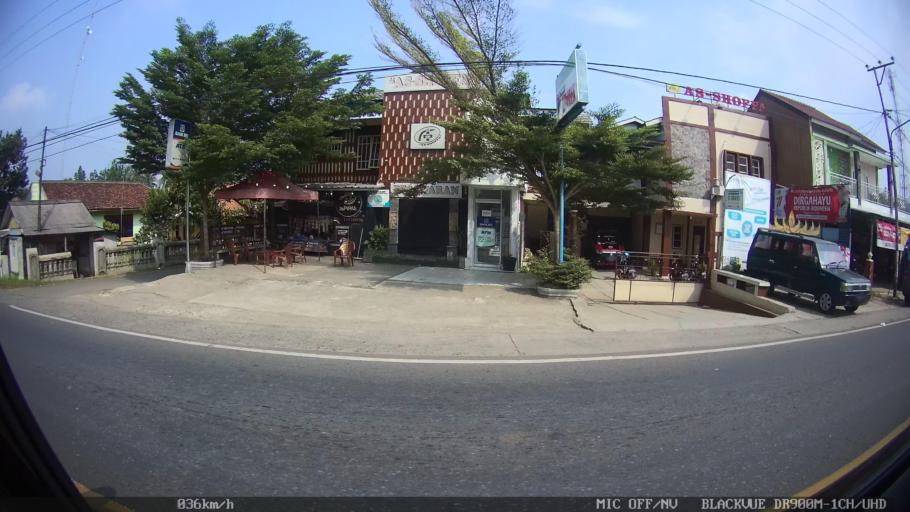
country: ID
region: Lampung
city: Gedongtataan
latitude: -5.3765
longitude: 105.1279
